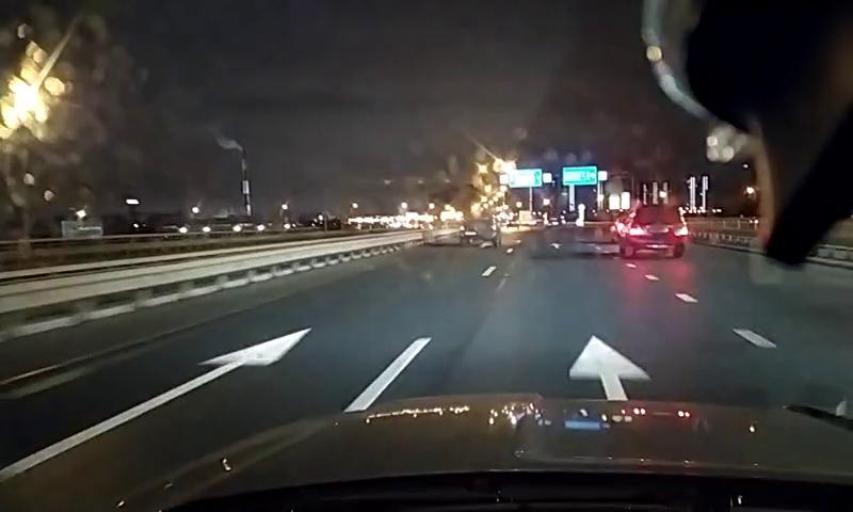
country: RU
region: Leningrad
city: Parnas
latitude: 60.0918
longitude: 30.3683
